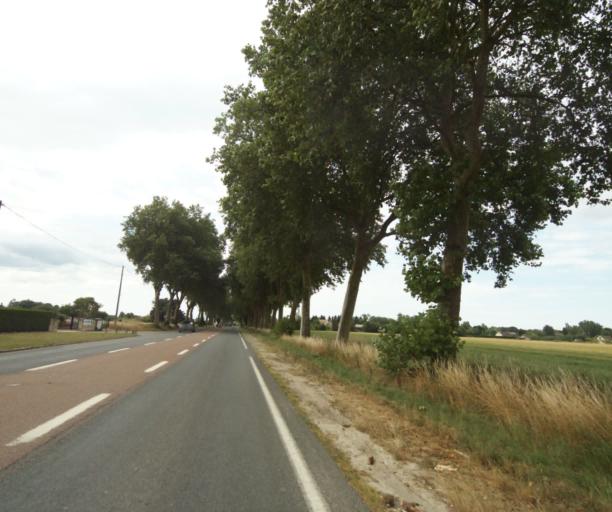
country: FR
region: Ile-de-France
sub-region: Departement de Seine-et-Marne
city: Chailly-en-Biere
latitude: 48.4580
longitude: 2.6140
